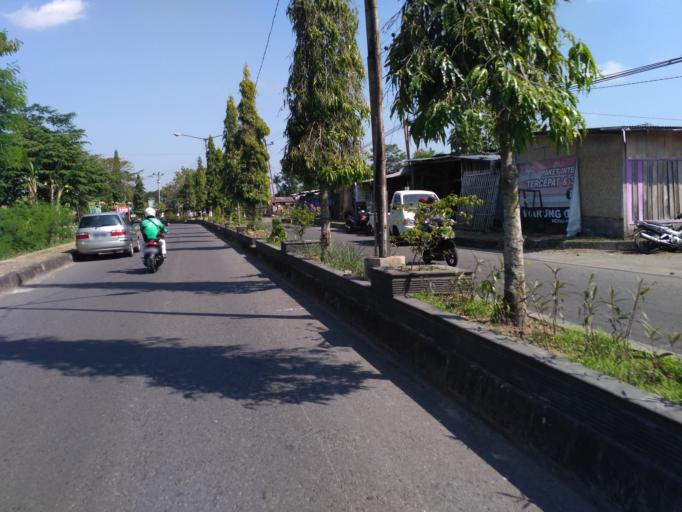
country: ID
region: Daerah Istimewa Yogyakarta
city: Depok
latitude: -7.7512
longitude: 110.4307
